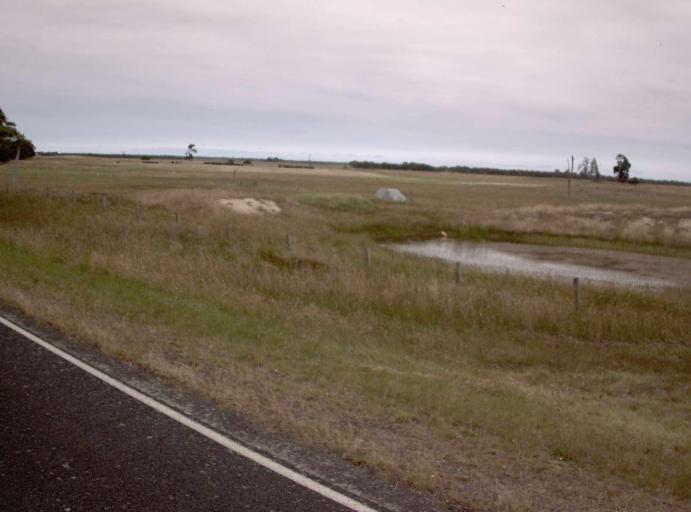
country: AU
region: Victoria
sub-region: Wellington
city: Sale
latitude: -38.5368
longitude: 146.9078
